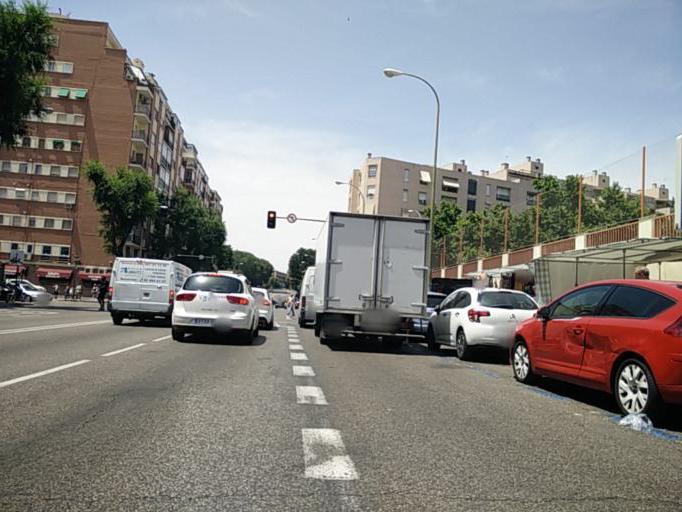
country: ES
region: Madrid
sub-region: Provincia de Madrid
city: Madrid
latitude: 40.4056
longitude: -3.7064
